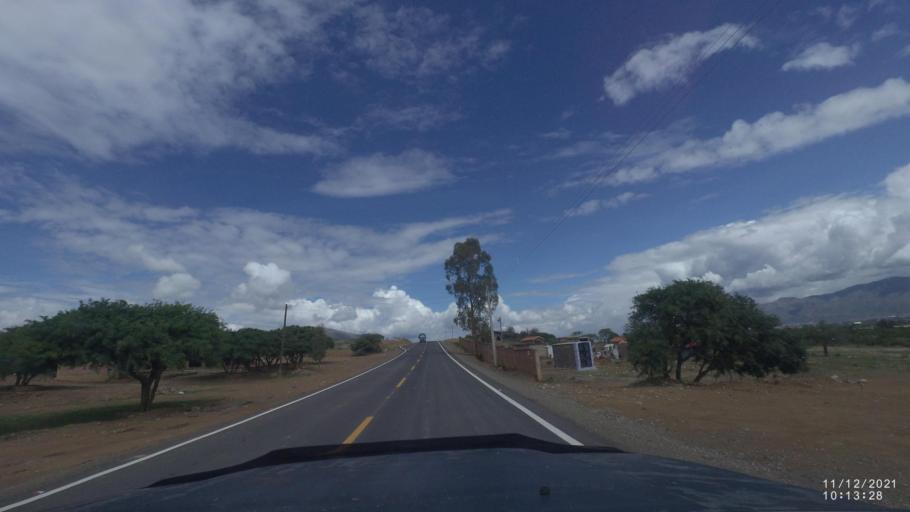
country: BO
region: Cochabamba
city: Tarata
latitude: -17.6231
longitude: -66.0086
